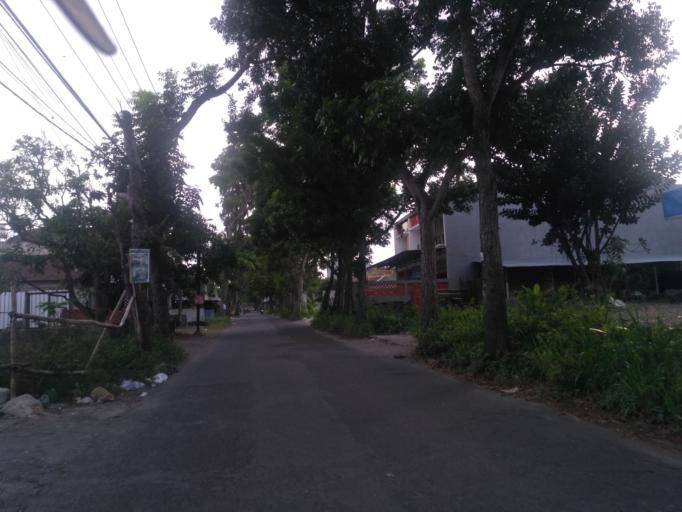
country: ID
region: Daerah Istimewa Yogyakarta
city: Yogyakarta
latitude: -7.7727
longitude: 110.3426
